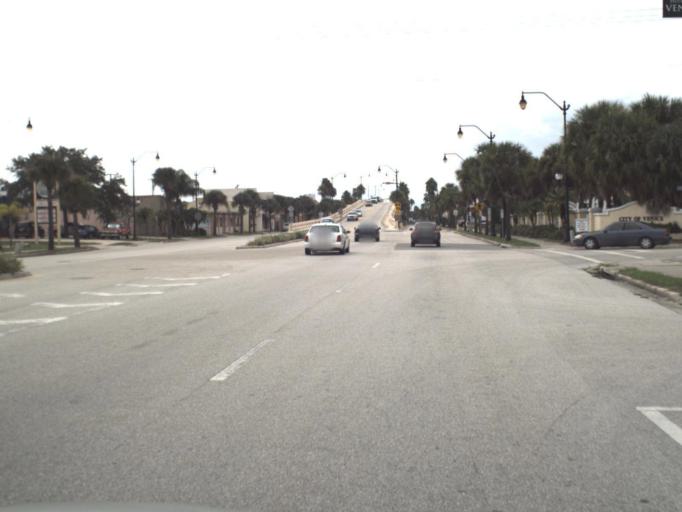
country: US
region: Florida
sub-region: Sarasota County
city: Venice
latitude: 27.0999
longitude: -82.4363
